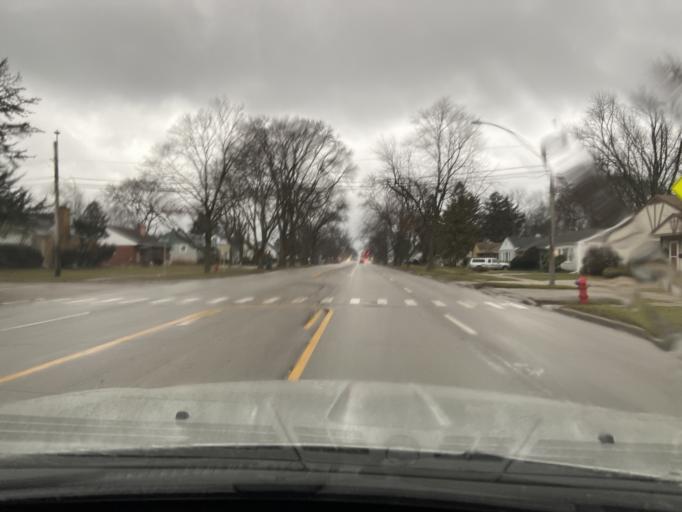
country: US
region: Illinois
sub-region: Cook County
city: Des Plaines
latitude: 42.0348
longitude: -87.9091
